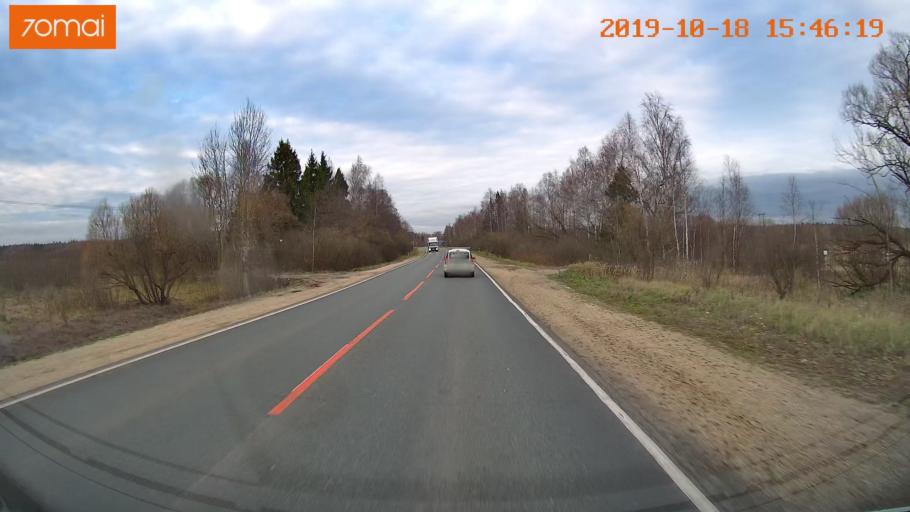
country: RU
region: Vladimir
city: Golovino
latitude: 56.0059
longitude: 40.5692
